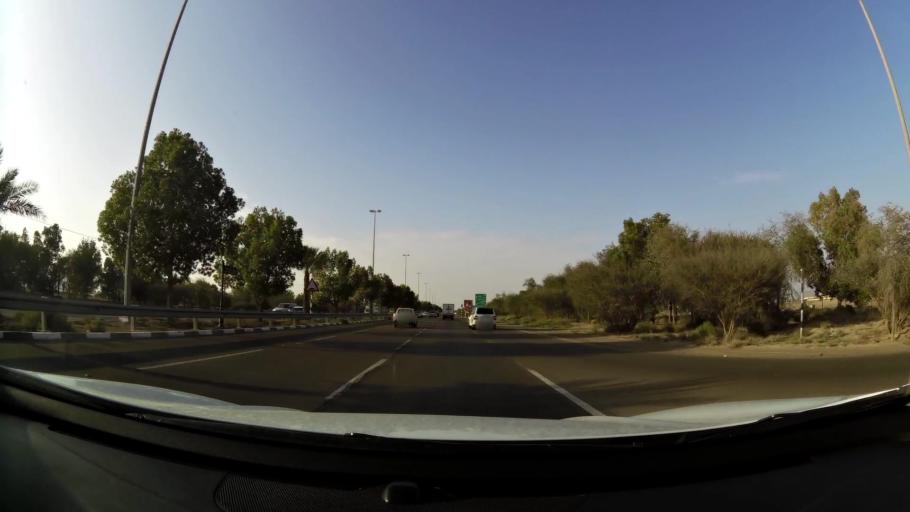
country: AE
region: Abu Dhabi
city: Al Ain
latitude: 24.1065
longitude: 55.8267
